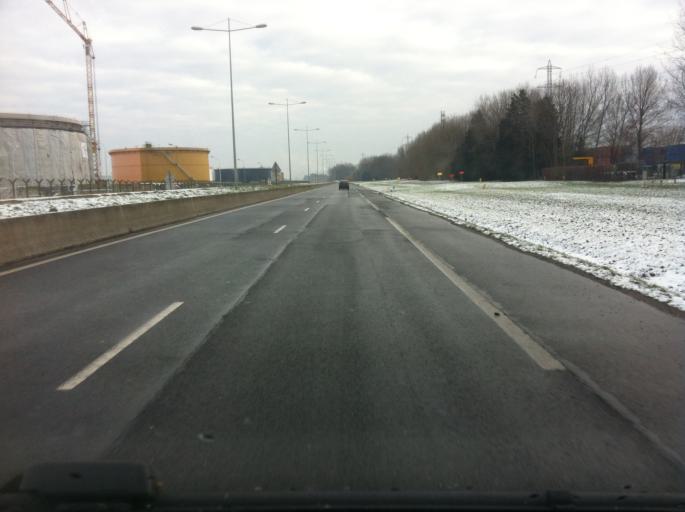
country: FR
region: Haute-Normandie
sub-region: Departement de la Seine-Maritime
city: Harfleur
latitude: 49.4845
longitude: 0.2276
